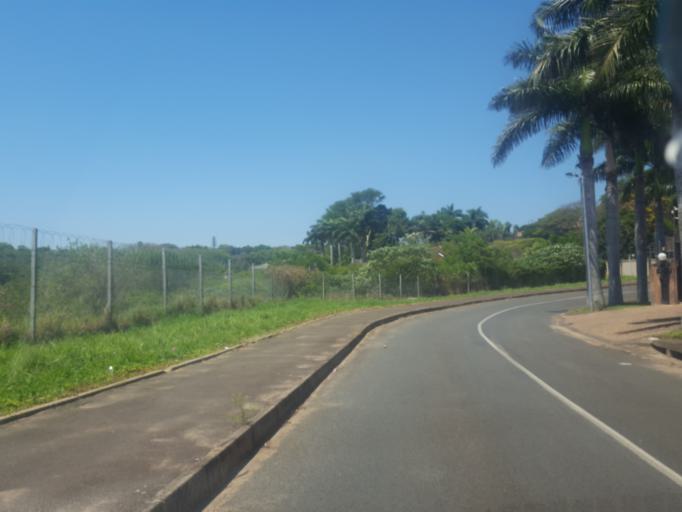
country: ZA
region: KwaZulu-Natal
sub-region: uThungulu District Municipality
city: Empangeni
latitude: -28.7432
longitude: 31.9032
